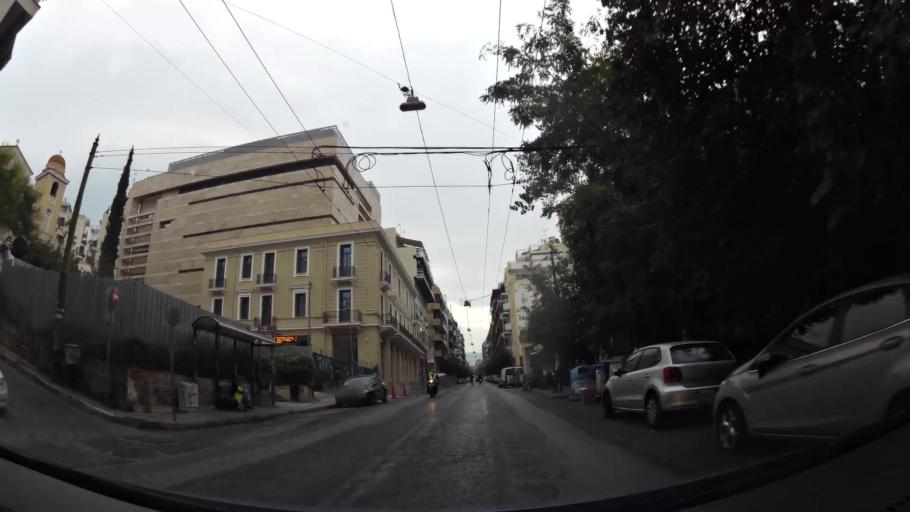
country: GR
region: Attica
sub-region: Nomarchia Athinas
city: Vyronas
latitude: 37.9700
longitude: 23.7424
